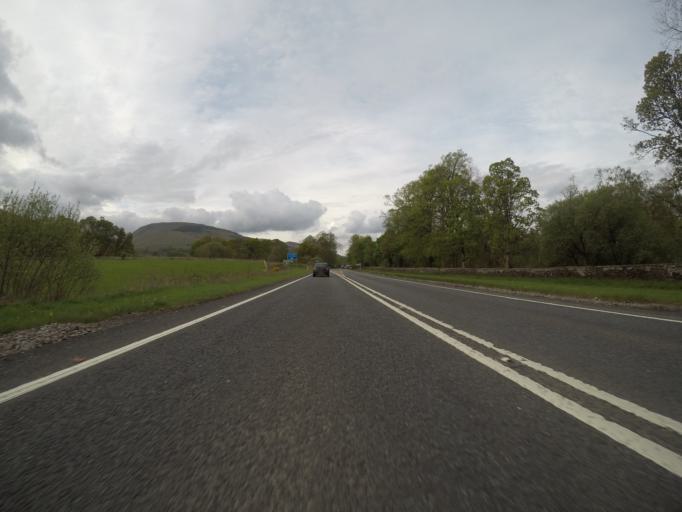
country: GB
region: Scotland
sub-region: West Dunbartonshire
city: Balloch
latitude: 56.0479
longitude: -4.6468
